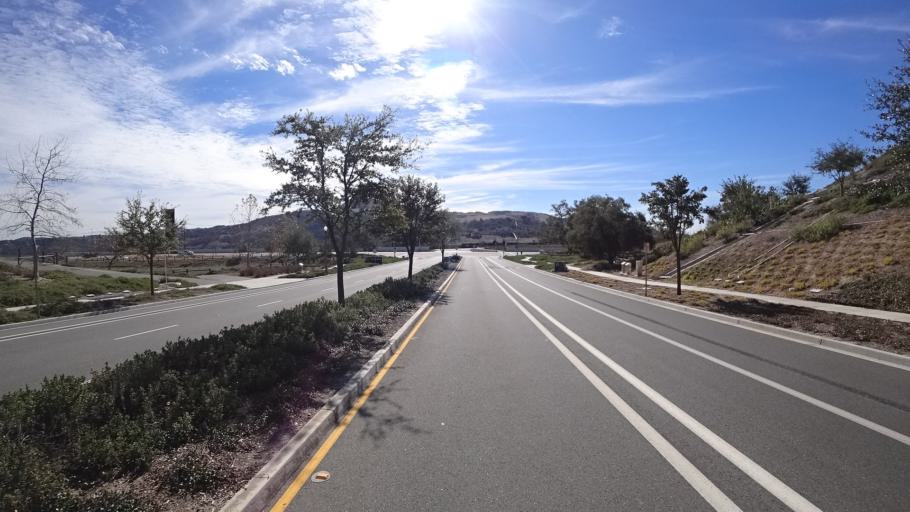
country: US
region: California
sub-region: Orange County
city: Ladera Ranch
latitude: 33.5291
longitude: -117.6013
